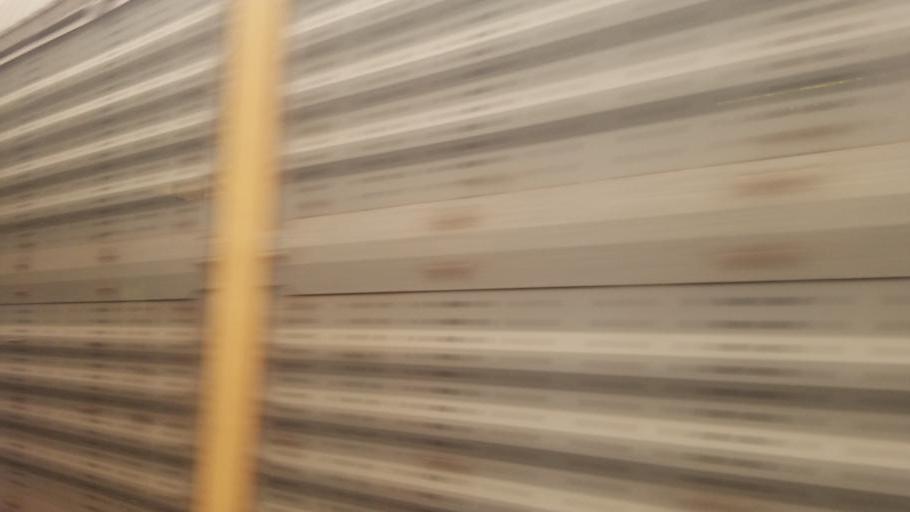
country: US
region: Pennsylvania
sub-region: Somerset County
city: Milford
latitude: 39.8821
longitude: -79.0954
